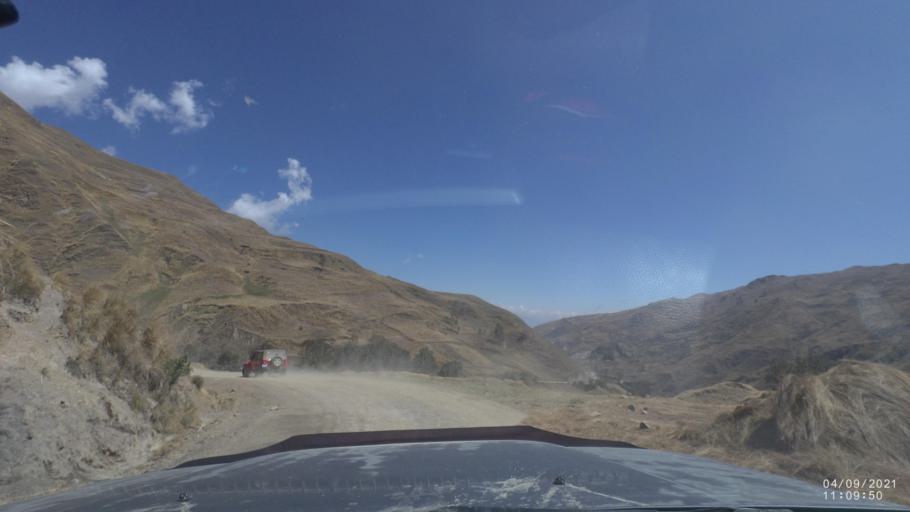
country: BO
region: Cochabamba
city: Sipe Sipe
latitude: -17.2781
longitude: -66.4799
